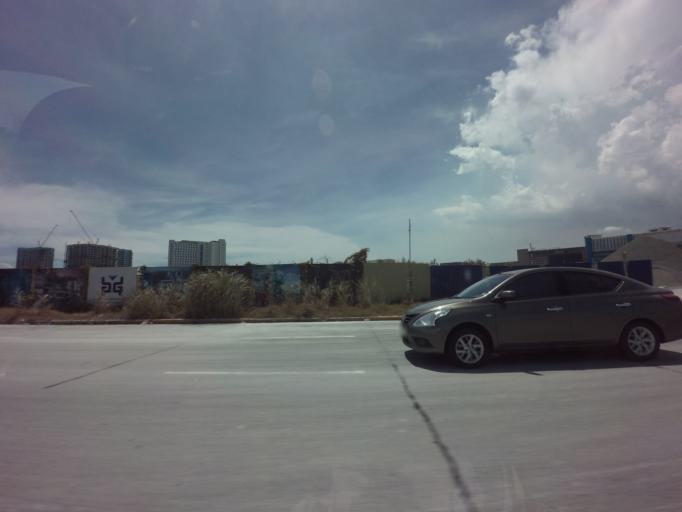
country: PH
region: Metro Manila
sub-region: Makati City
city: Makati City
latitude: 14.5174
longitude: 120.9851
